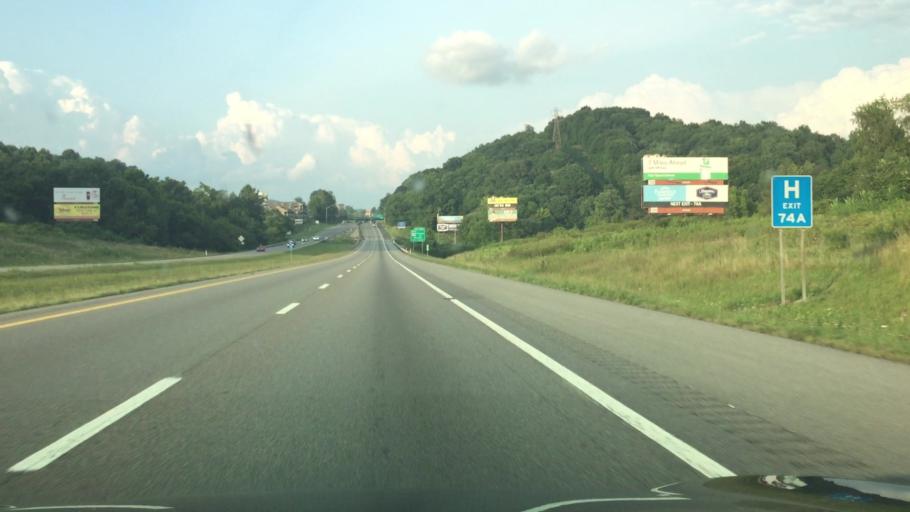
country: US
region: Tennessee
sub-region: Sullivan County
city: Walnut Hill
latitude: 36.5822
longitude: -82.2690
